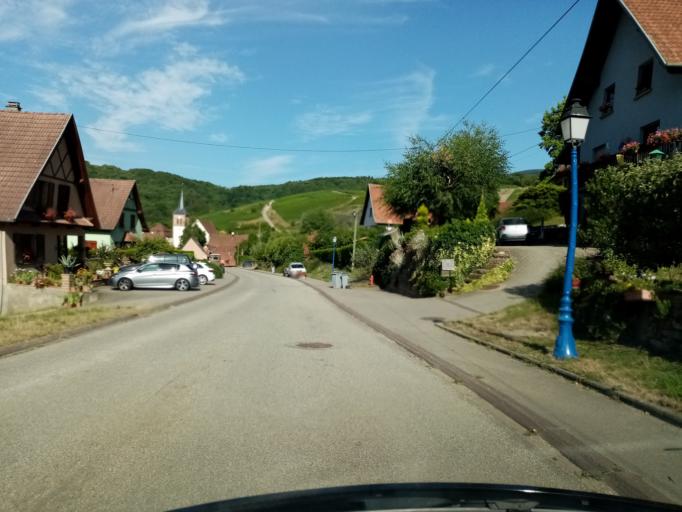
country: FR
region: Alsace
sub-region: Departement du Bas-Rhin
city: Ville
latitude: 48.3561
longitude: 7.3216
